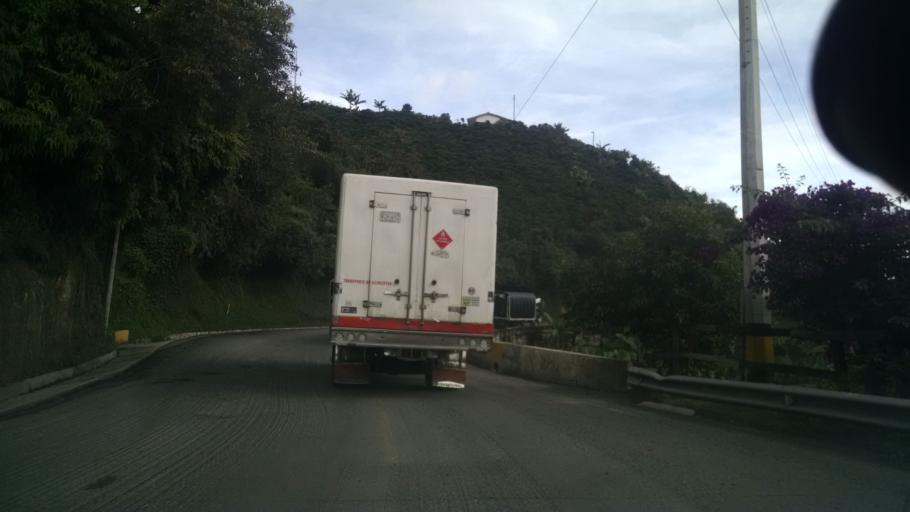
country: CO
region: Antioquia
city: Santa Barbara
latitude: 5.9024
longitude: -75.5750
